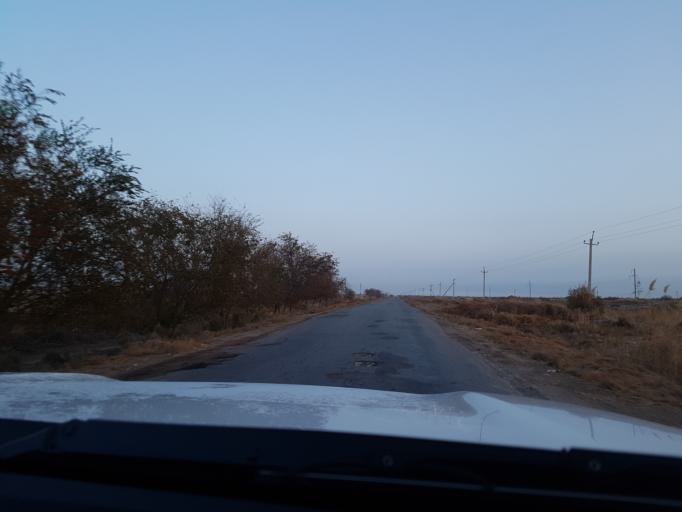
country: TM
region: Dasoguz
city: Koeneuergench
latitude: 41.7688
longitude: 58.6936
